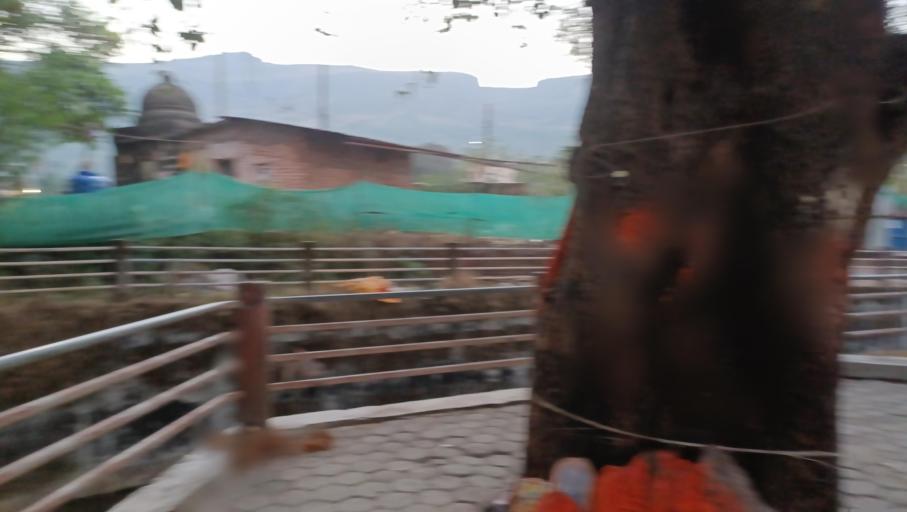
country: IN
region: Maharashtra
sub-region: Nashik Division
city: Trimbak
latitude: 19.9318
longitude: 73.5306
